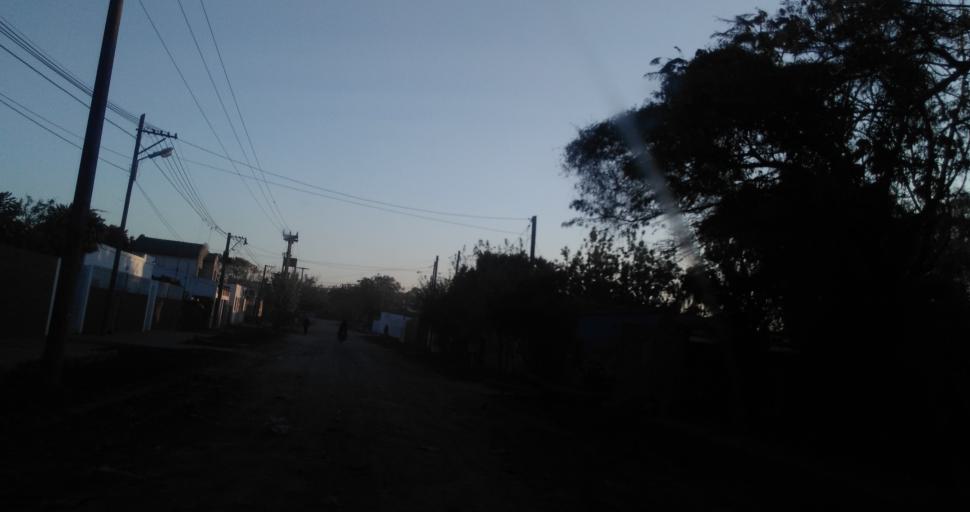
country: AR
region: Chaco
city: Fontana
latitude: -27.4285
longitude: -59.0065
